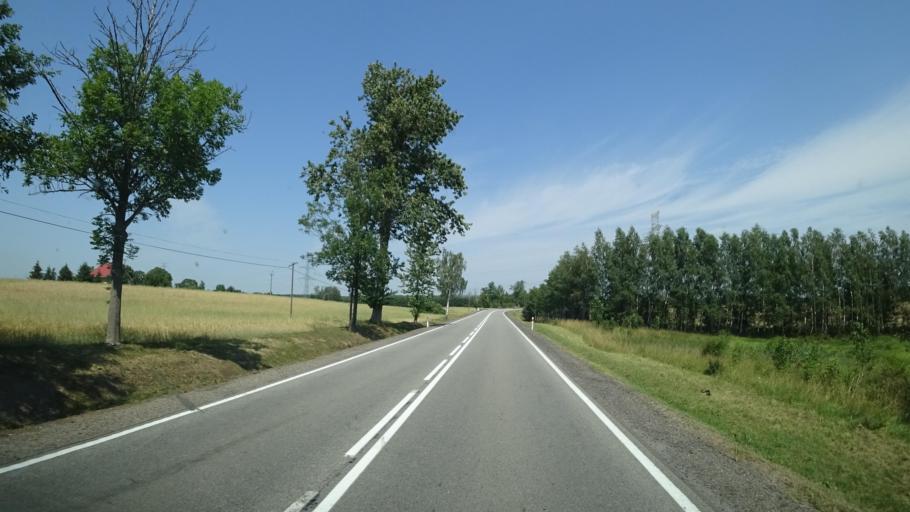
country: PL
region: Pomeranian Voivodeship
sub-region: Powiat koscierski
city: Koscierzyna
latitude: 54.1529
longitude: 18.0307
